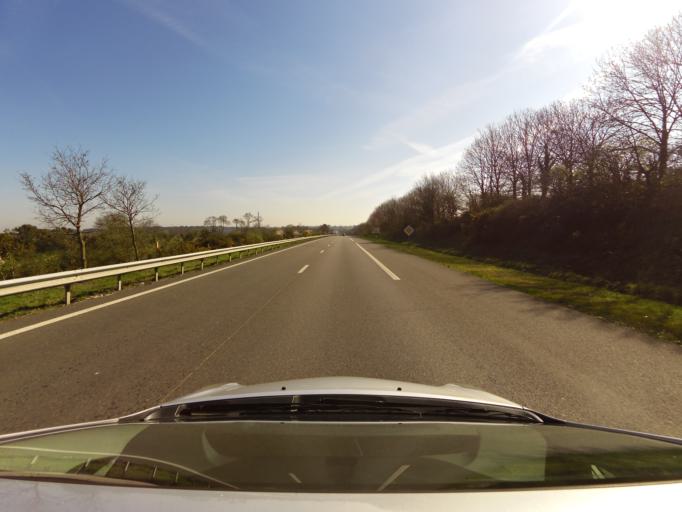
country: FR
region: Brittany
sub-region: Departement d'Ille-et-Vilaine
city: Saint-Thurial
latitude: 48.0407
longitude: -1.9526
